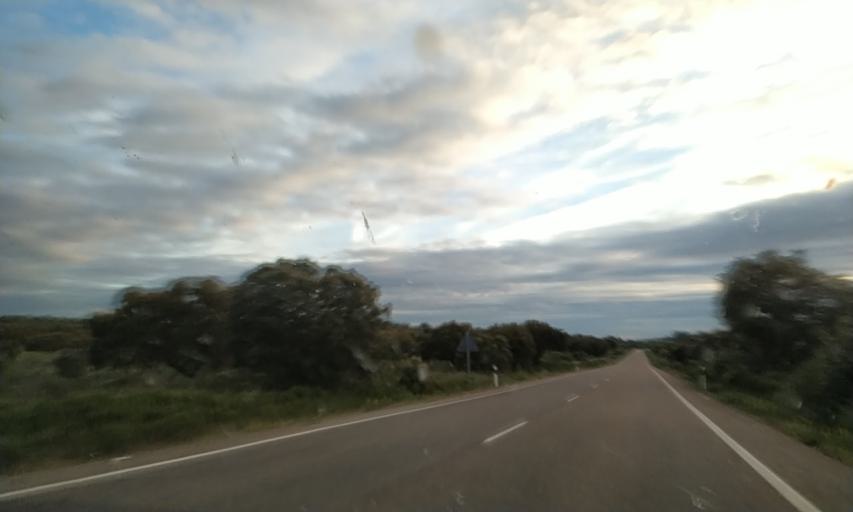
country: ES
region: Extremadura
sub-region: Provincia de Badajoz
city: La Roca de la Sierra
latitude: 39.1231
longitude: -6.6709
